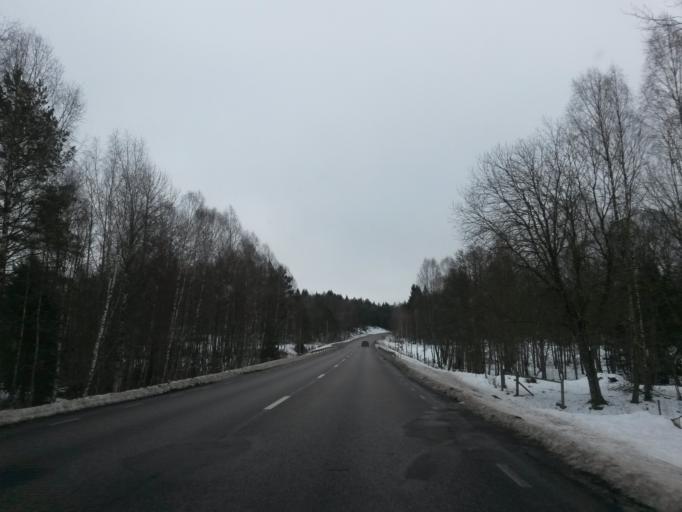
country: SE
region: Vaestra Goetaland
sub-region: Herrljunga Kommun
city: Herrljunga
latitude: 57.9658
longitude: 13.1546
